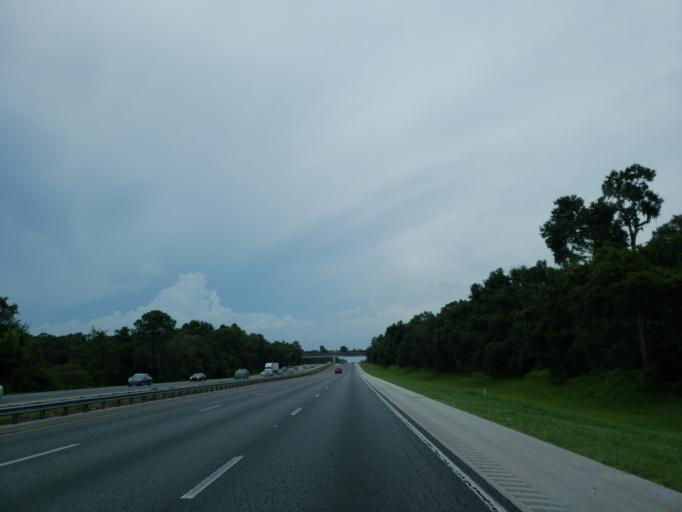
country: US
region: Florida
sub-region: Marion County
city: Belleview
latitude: 29.0414
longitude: -82.1644
